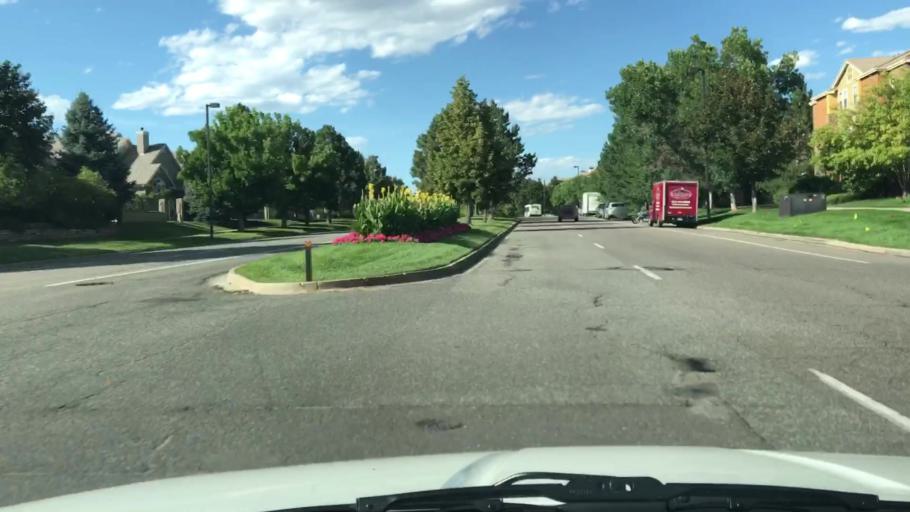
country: US
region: Colorado
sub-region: Arapahoe County
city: Greenwood Village
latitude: 39.6306
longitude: -104.9112
